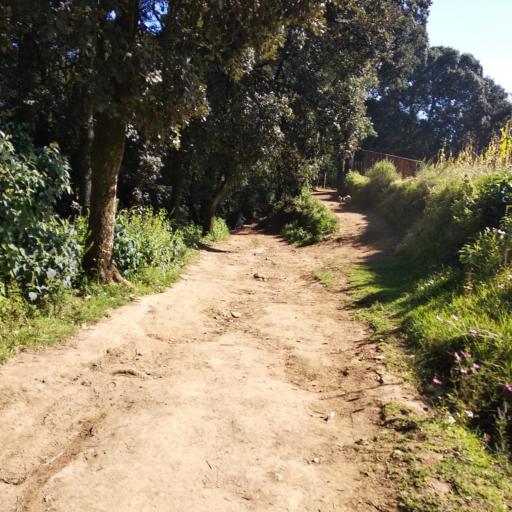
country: MX
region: Mexico City
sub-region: Tlalpan
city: Lomas de Tepemecatl
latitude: 19.2850
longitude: -99.2672
